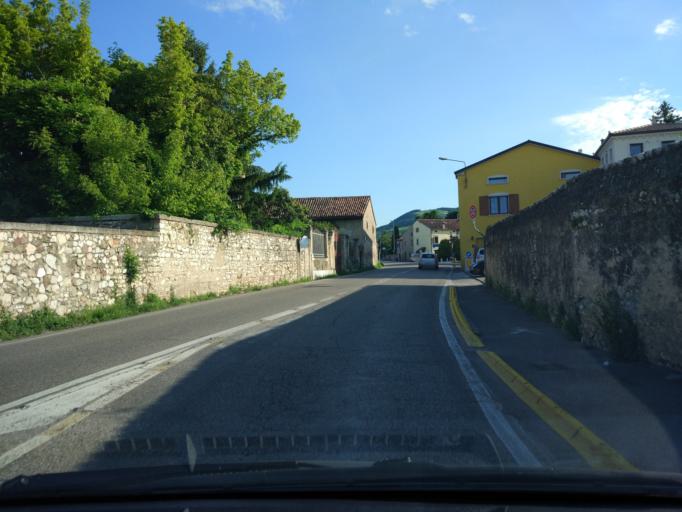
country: IT
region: Veneto
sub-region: Provincia di Verona
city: Illasi
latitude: 45.4720
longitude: 11.1809
